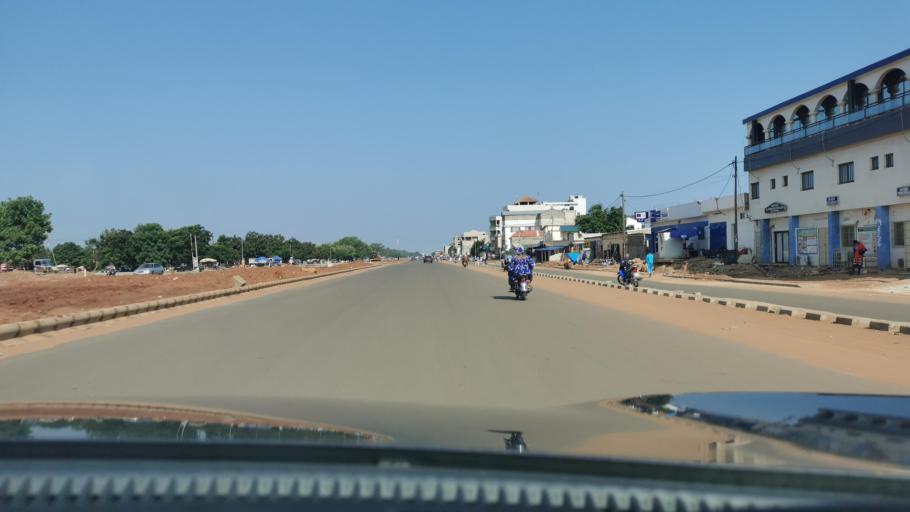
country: TG
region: Maritime
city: Lome
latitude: 6.1985
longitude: 1.1510
